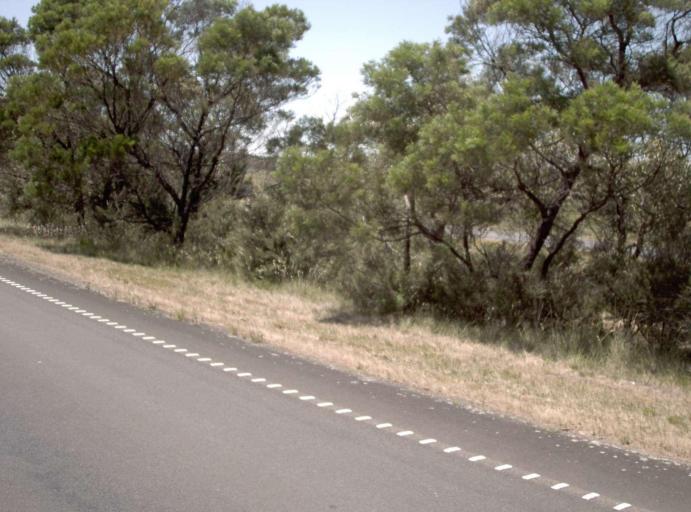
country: AU
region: Victoria
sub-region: Cardinia
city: Bunyip
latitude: -38.0774
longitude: 145.7074
